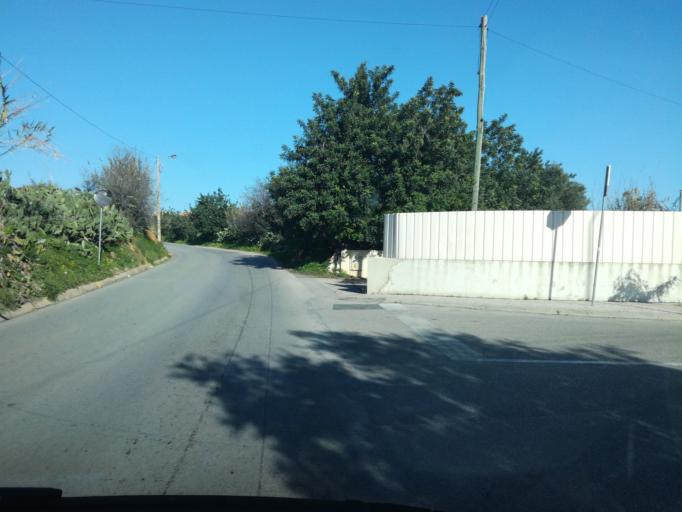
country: PT
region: Faro
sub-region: Olhao
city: Olhao
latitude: 37.0379
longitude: -7.8327
